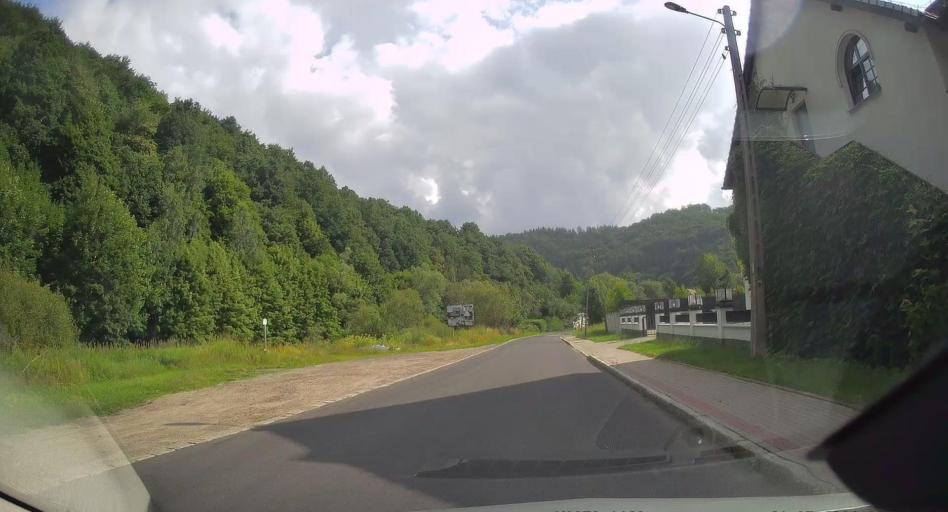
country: PL
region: Lower Silesian Voivodeship
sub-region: Powiat walbrzyski
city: Walim
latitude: 50.7390
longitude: 16.4053
